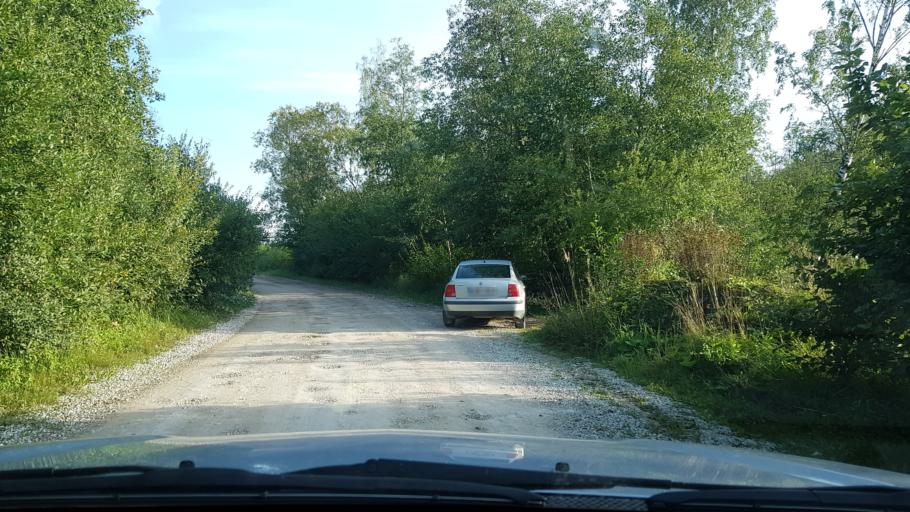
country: EE
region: Ida-Virumaa
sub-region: Sillamaee linn
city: Sillamae
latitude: 59.2714
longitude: 27.9218
